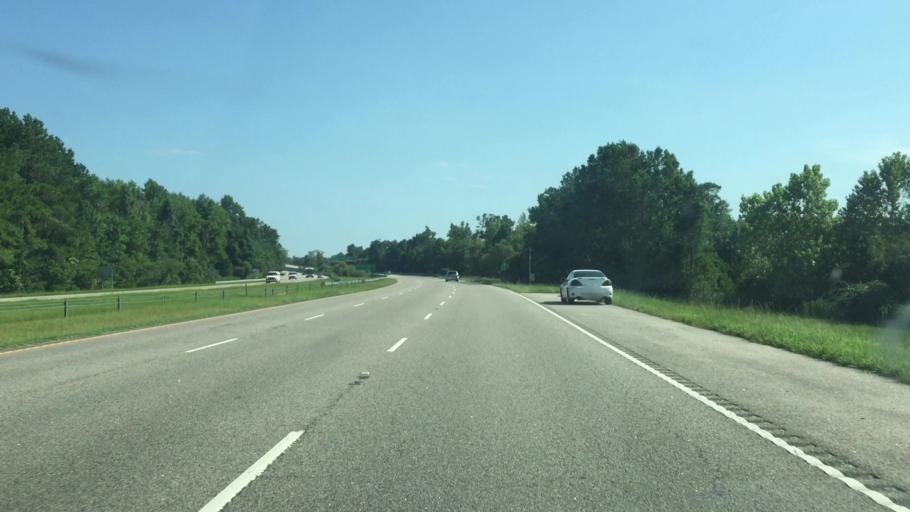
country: US
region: South Carolina
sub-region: Horry County
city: North Myrtle Beach
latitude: 33.8000
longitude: -78.7794
